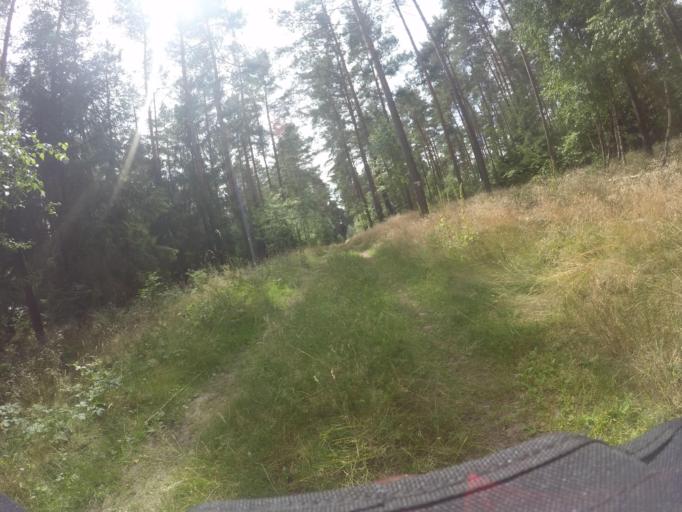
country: DE
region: Lower Saxony
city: Dahlem
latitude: 53.2347
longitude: 10.7258
